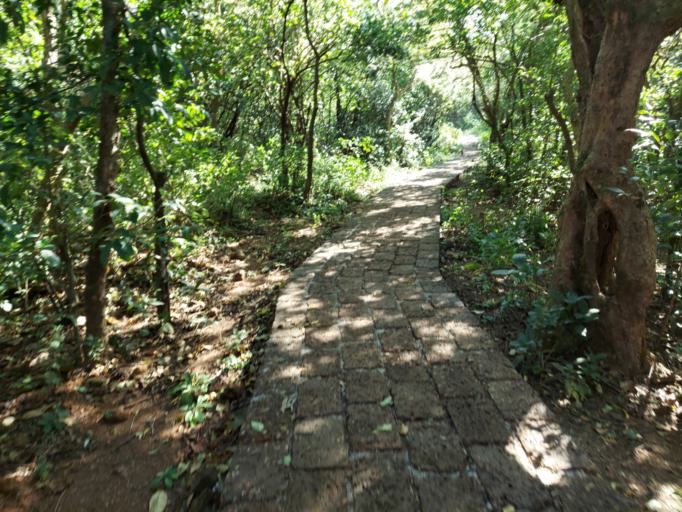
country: IN
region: Maharashtra
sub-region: Sindhudurg
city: Kudal
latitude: 16.0831
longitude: 73.8443
